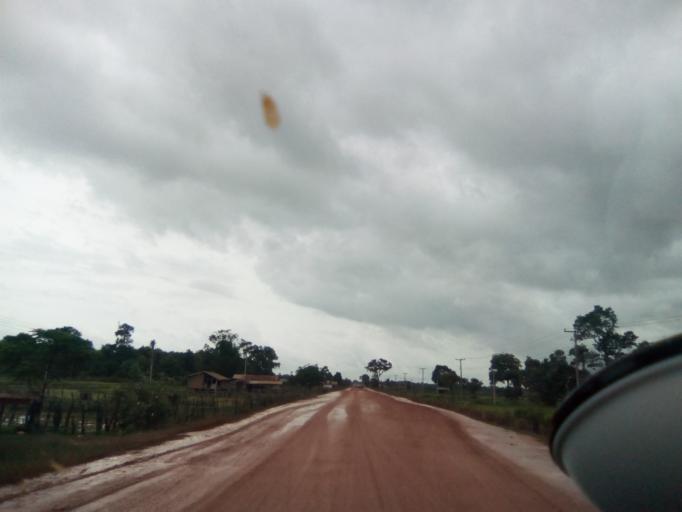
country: LA
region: Attapu
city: Attapu
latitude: 14.7604
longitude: 106.7114
